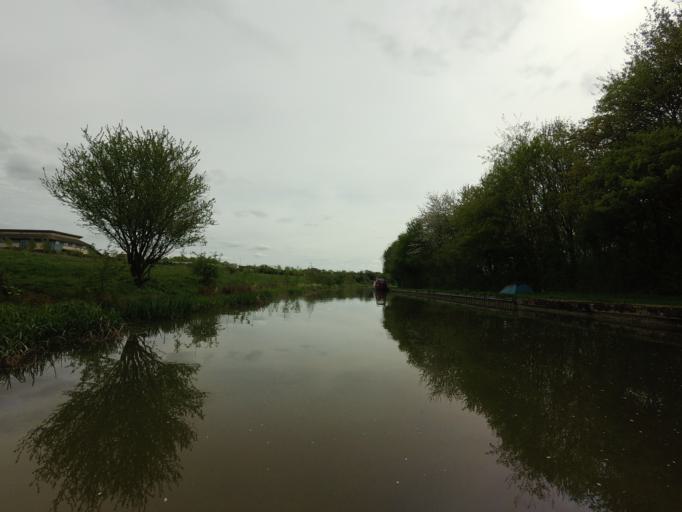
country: GB
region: England
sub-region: Milton Keynes
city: Bradwell
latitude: 52.0699
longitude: -0.7801
